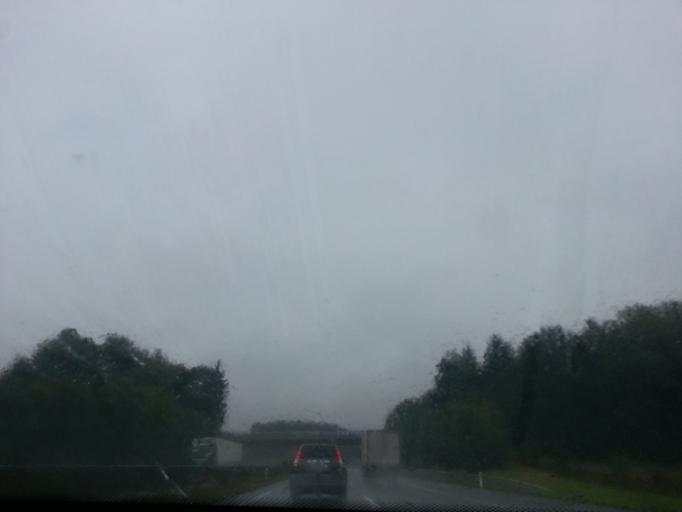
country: AT
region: Upper Austria
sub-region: Politischer Bezirk Vocklabruck
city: Desselbrunn
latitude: 47.9844
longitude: 13.7763
